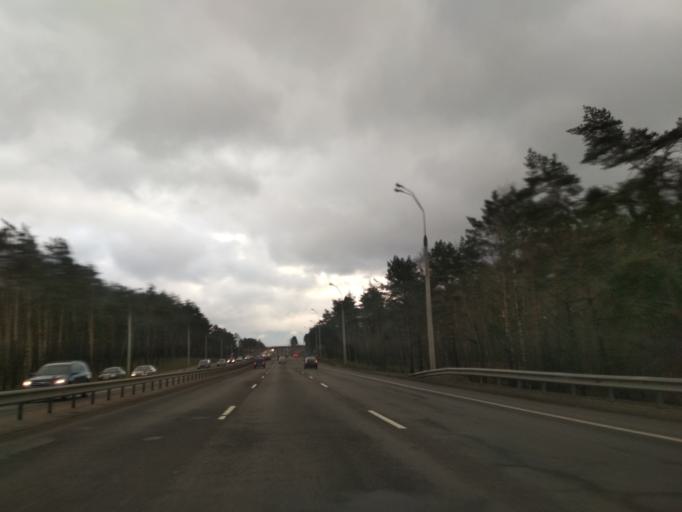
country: BY
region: Minsk
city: Vyaliki Trastsyanets
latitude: 53.8255
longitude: 27.7519
